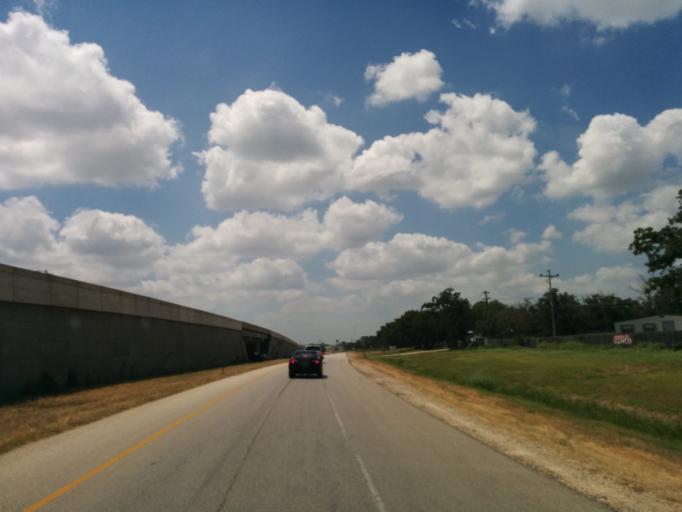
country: US
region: Texas
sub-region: Bastrop County
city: Wyldwood
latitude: 30.1122
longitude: -97.4139
